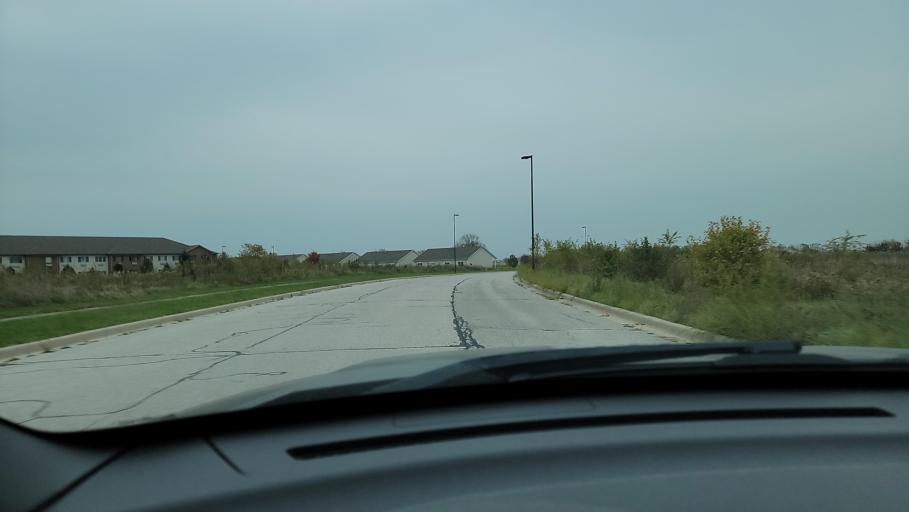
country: US
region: Indiana
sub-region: Porter County
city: Portage
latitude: 41.5450
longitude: -87.1750
